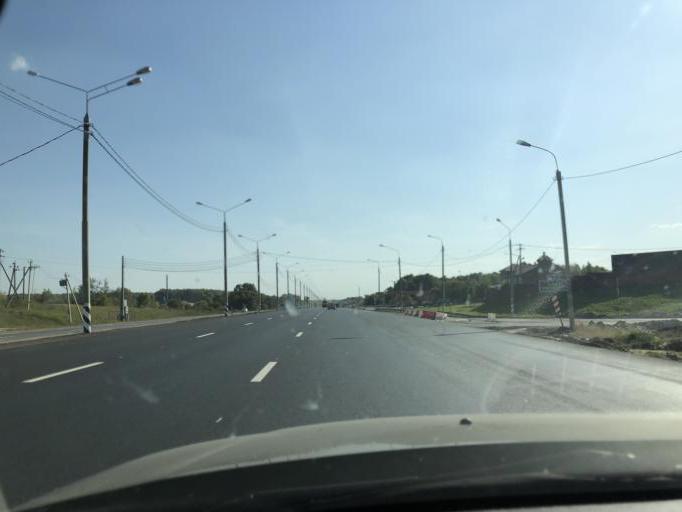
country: RU
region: Tula
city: Novogurovskiy
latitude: 54.4680
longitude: 37.5112
